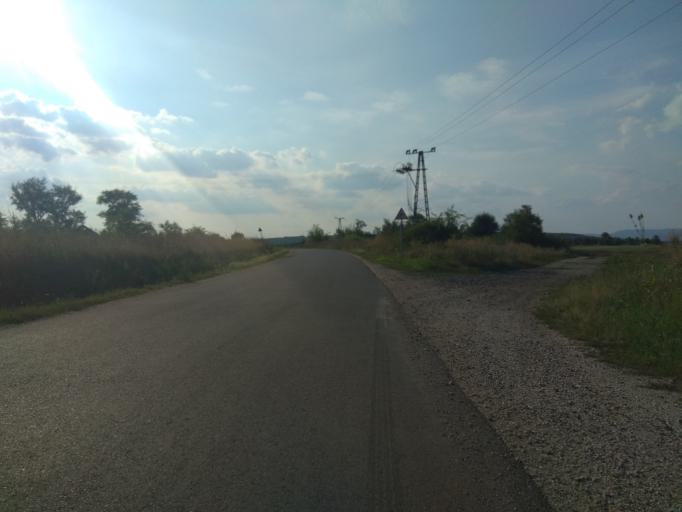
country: HU
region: Borsod-Abauj-Zemplen
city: Harsany
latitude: 47.8972
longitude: 20.7485
